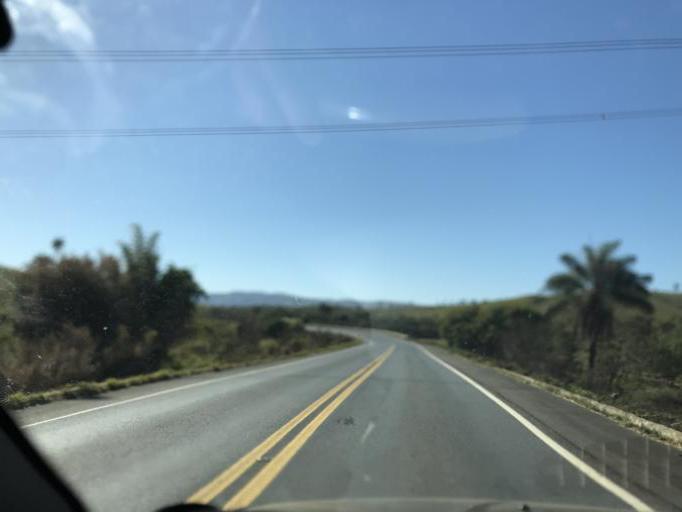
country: BR
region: Minas Gerais
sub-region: Bambui
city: Bambui
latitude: -19.8428
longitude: -45.9995
